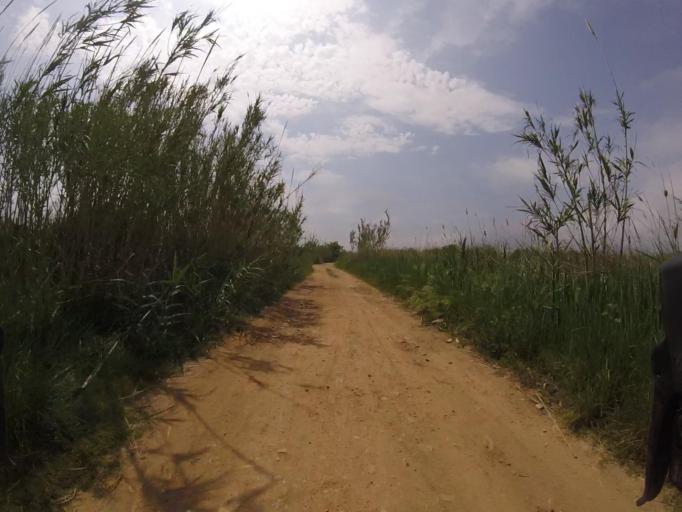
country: ES
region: Valencia
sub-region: Provincia de Castello
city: Orpesa/Oropesa del Mar
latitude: 40.1575
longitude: 0.1724
